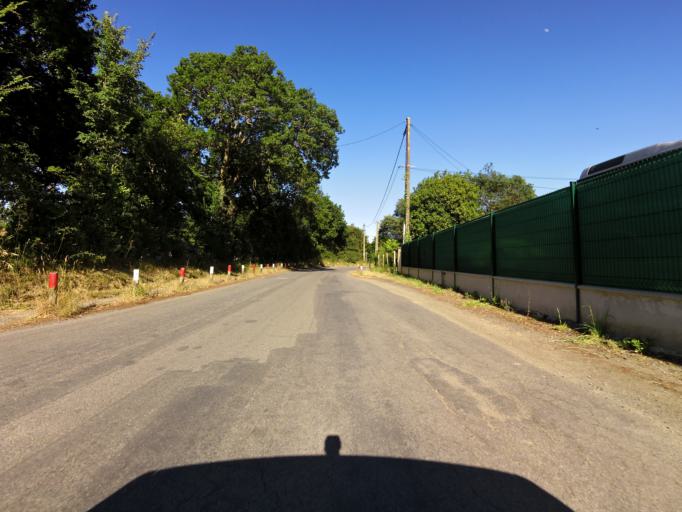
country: FR
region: Brittany
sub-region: Departement du Morbihan
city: Penestin
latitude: 47.4641
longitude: -2.4837
